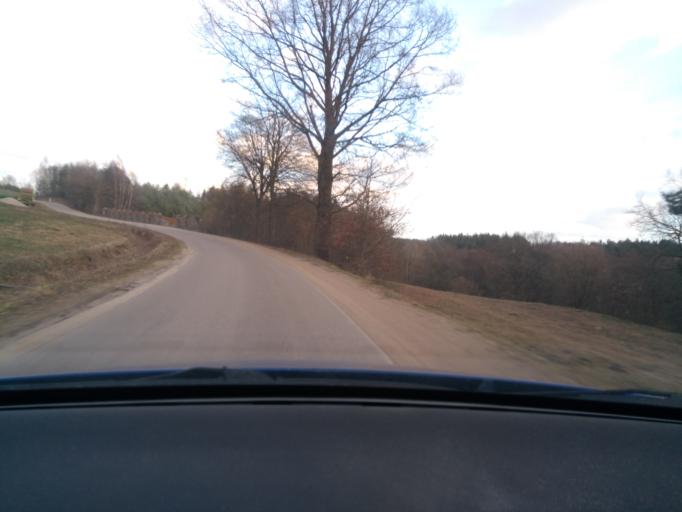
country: PL
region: Pomeranian Voivodeship
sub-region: Powiat kartuski
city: Przodkowo
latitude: 54.4135
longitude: 18.2512
